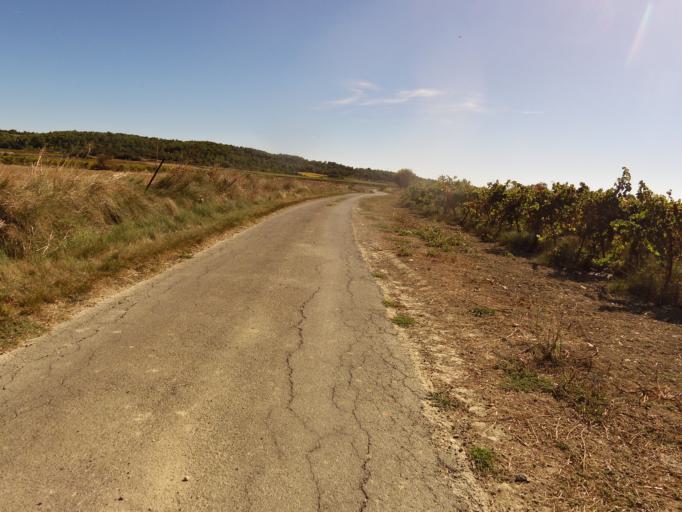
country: FR
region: Languedoc-Roussillon
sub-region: Departement du Gard
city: Nages-et-Solorgues
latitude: 43.7765
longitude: 4.2177
